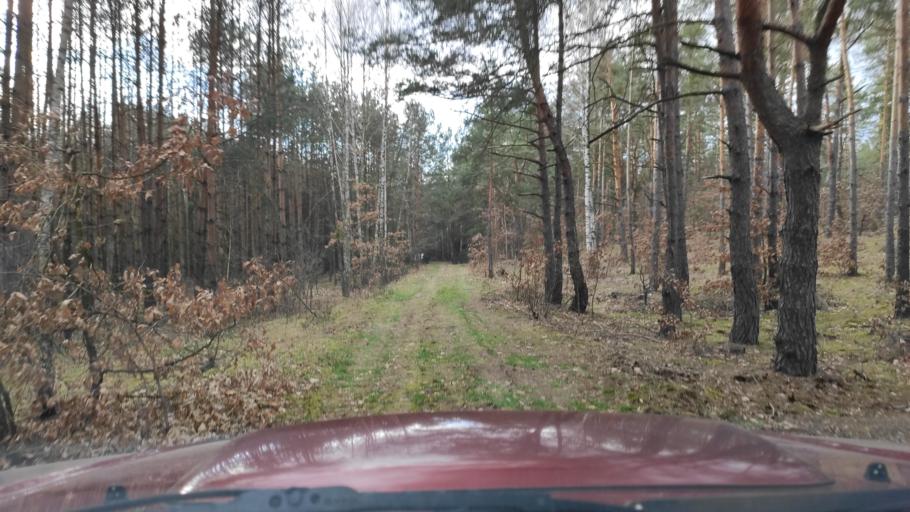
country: PL
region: Masovian Voivodeship
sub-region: Powiat kozienicki
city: Garbatka-Letnisko
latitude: 51.5117
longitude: 21.5747
